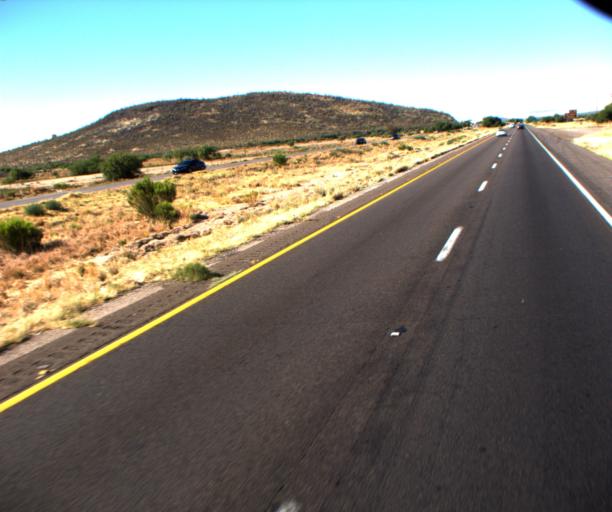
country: US
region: Arizona
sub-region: Pima County
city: Drexel Heights
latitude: 32.1175
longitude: -110.9899
